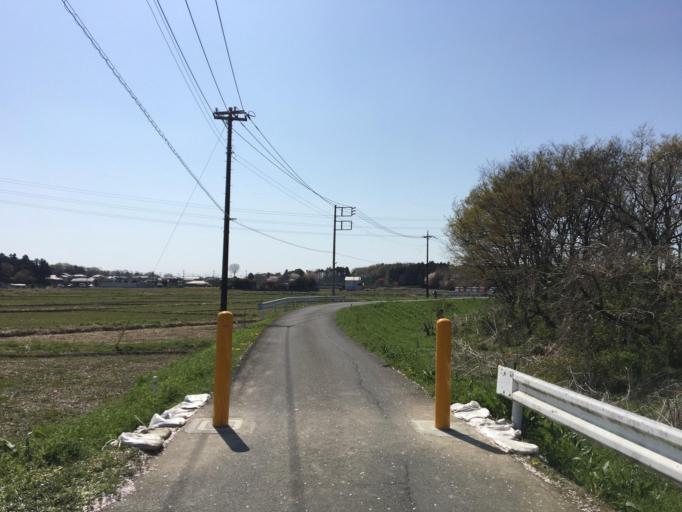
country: JP
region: Saitama
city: Sakado
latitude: 35.9632
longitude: 139.3442
